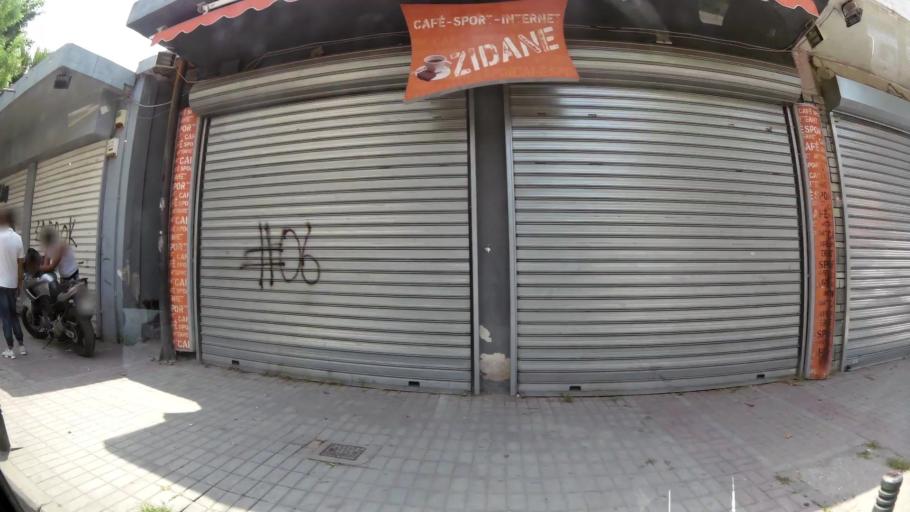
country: GR
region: Central Macedonia
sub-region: Nomos Thessalonikis
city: Menemeni
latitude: 40.6584
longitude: 22.8972
